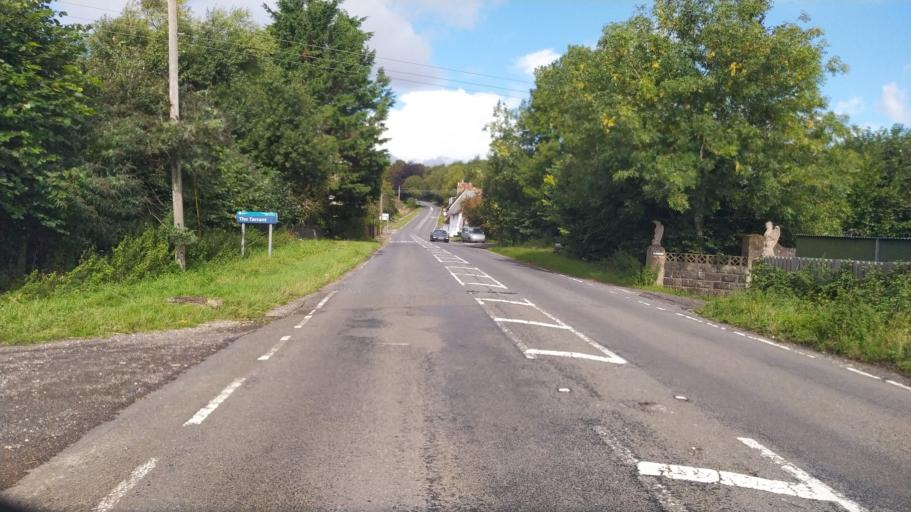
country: GB
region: England
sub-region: Dorset
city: Blandford Forum
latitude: 50.8401
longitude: -2.0960
